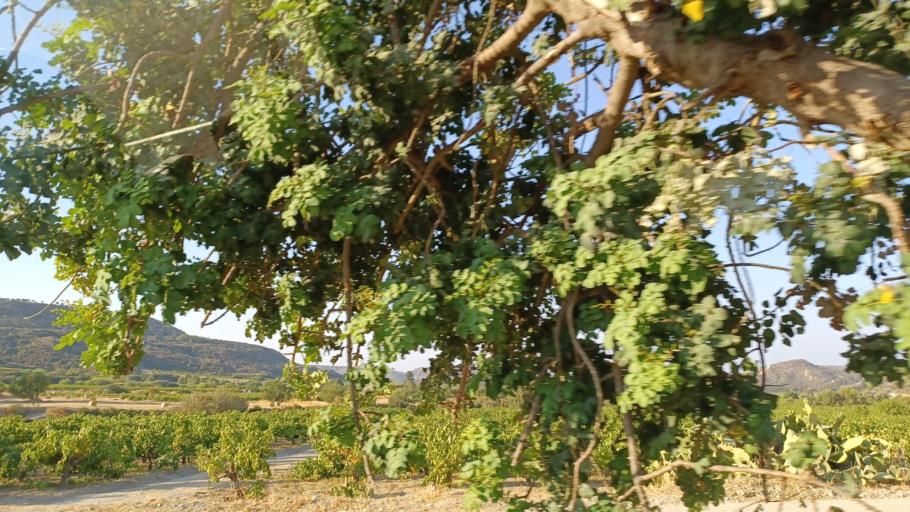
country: CY
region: Limassol
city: Pissouri
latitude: 34.7108
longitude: 32.6792
